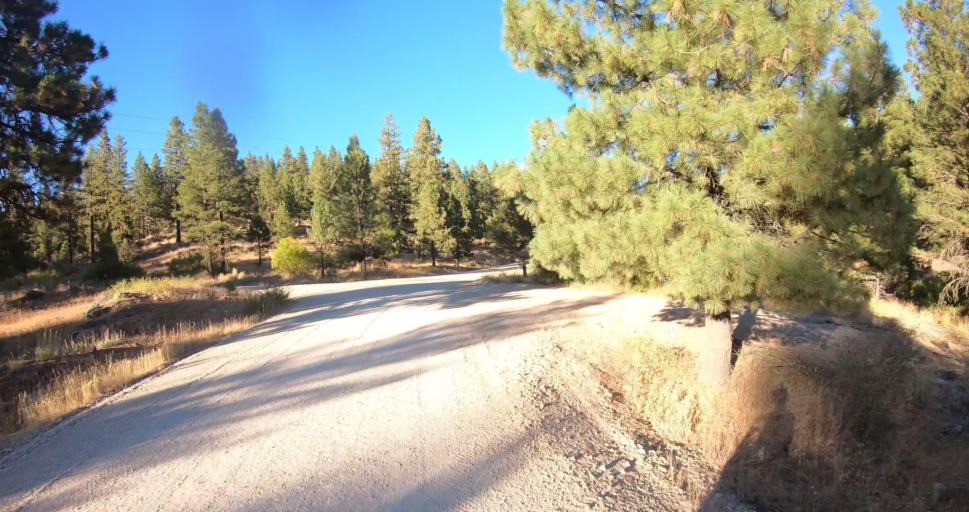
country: US
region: Oregon
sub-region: Lake County
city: Lakeview
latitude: 42.1994
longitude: -120.3042
